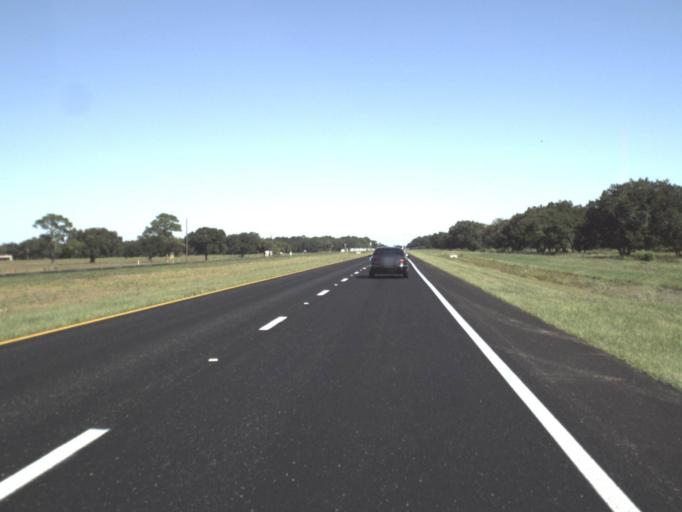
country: US
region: Florida
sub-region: Hendry County
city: Port LaBelle
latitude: 26.7683
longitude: -81.3451
